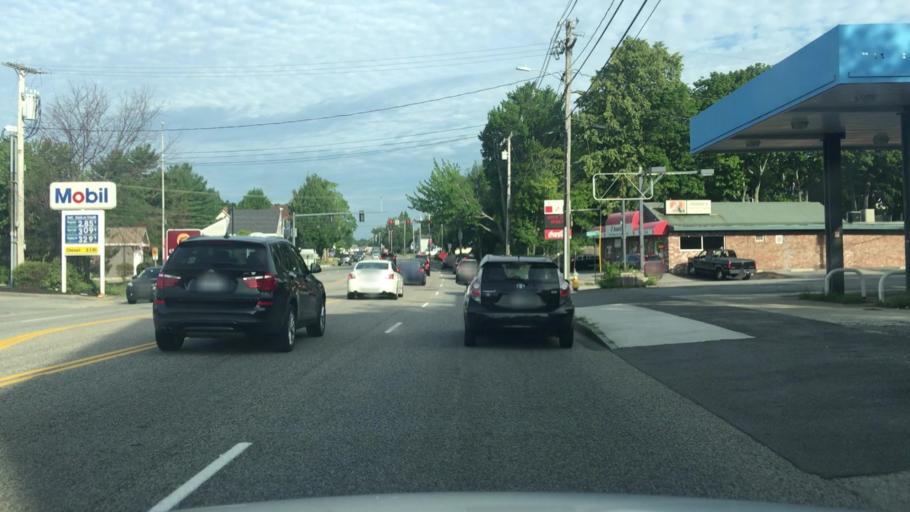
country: US
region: Maine
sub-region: Cumberland County
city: South Portland Gardens
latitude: 43.6572
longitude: -70.2894
